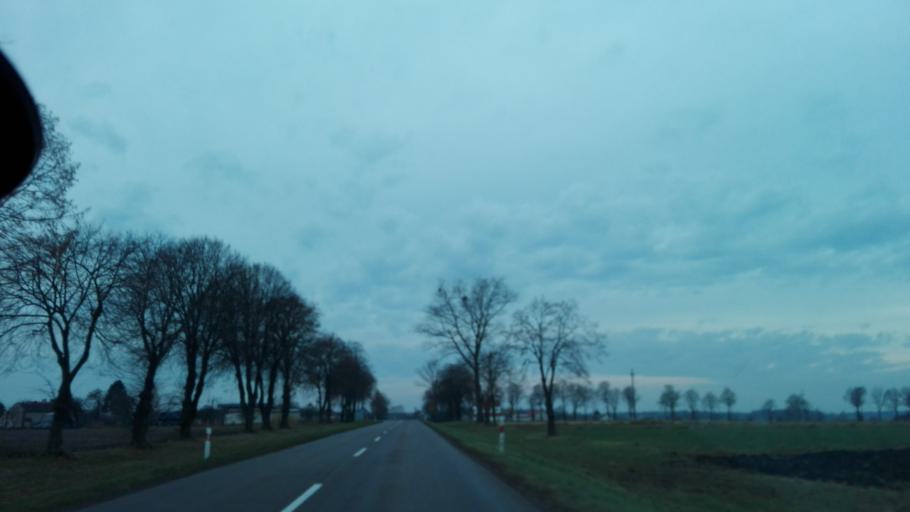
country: PL
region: Lublin Voivodeship
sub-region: Powiat radzynski
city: Wohyn
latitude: 51.7796
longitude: 22.7675
